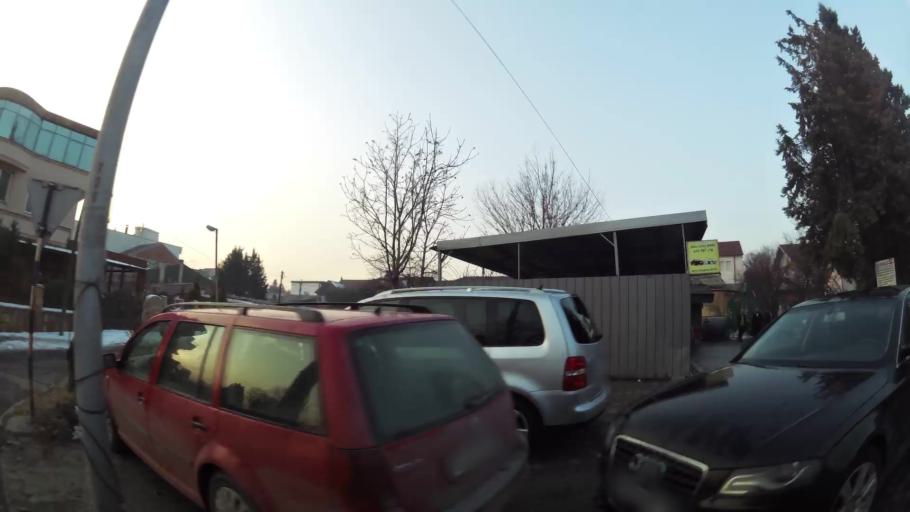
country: MK
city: Creshevo
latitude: 42.0090
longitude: 21.5081
